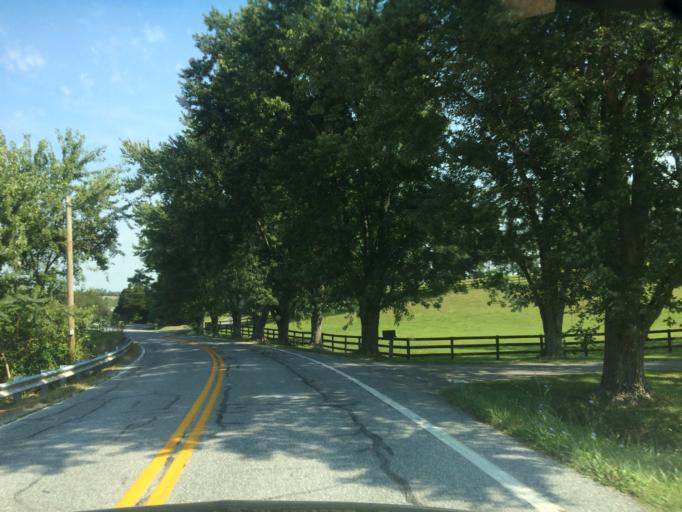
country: US
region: Maryland
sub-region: Carroll County
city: New Windsor
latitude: 39.6047
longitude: -77.1165
